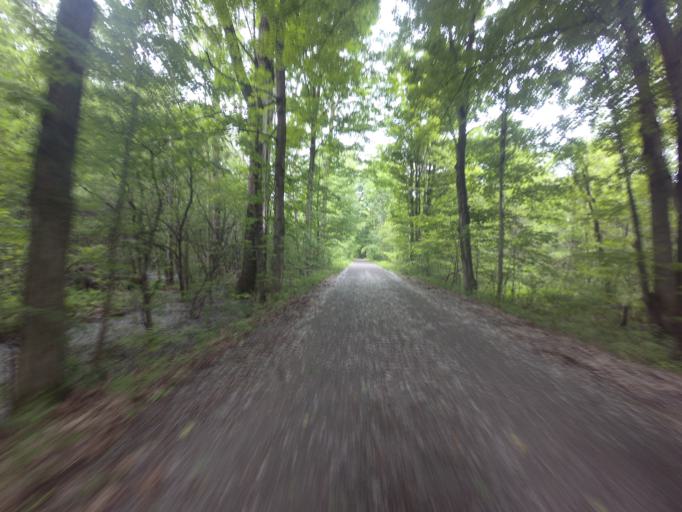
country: US
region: New York
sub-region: Jefferson County
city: Calcium
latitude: 43.9885
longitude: -75.8357
